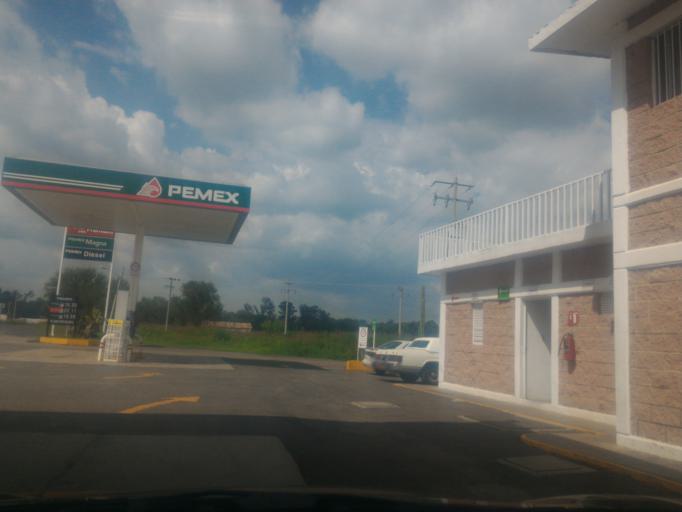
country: MX
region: Jalisco
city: San Diego de Alejandria
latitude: 20.8709
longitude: -101.9874
